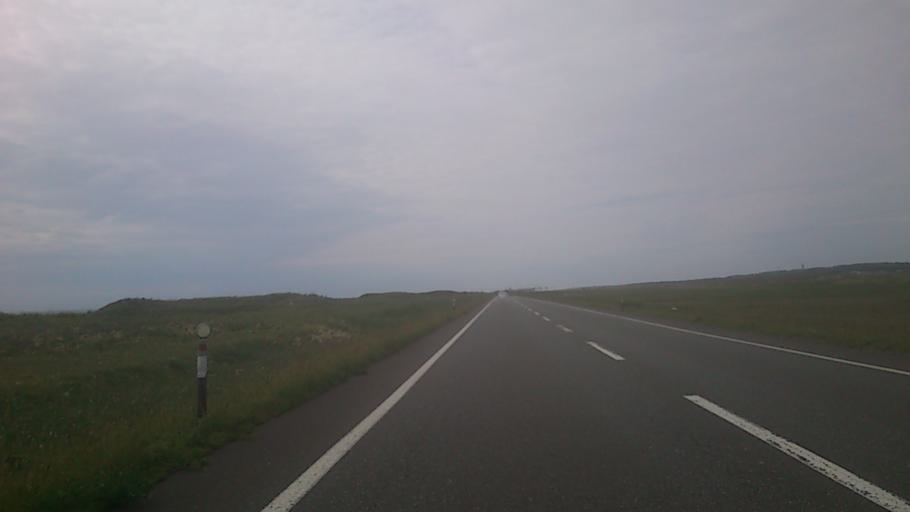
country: JP
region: Hokkaido
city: Wakkanai
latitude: 45.0692
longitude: 141.6413
